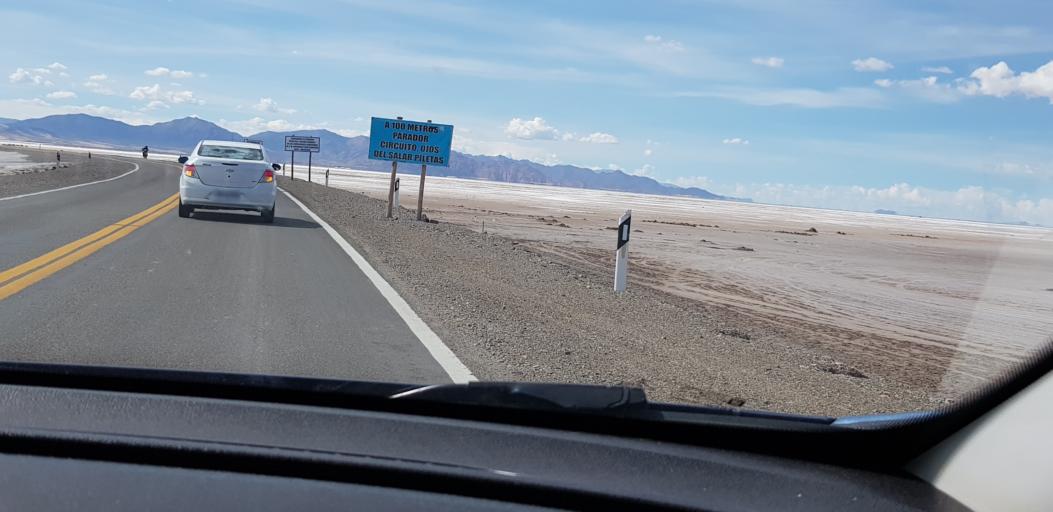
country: AR
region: Jujuy
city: El Aguilar
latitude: -23.6100
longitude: -65.8631
